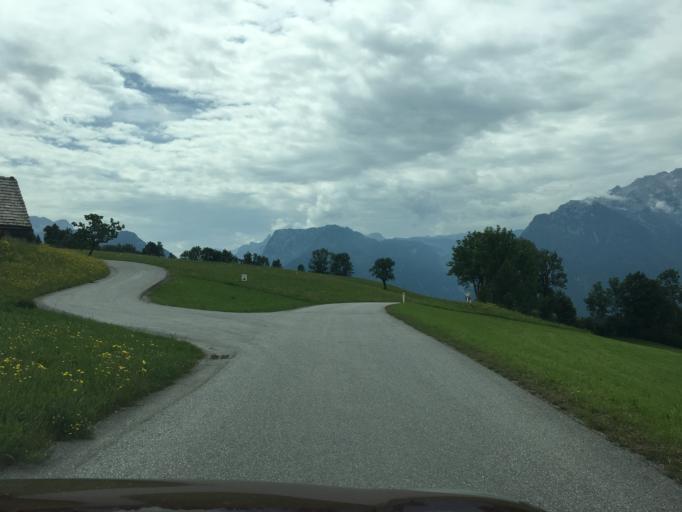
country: AT
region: Salzburg
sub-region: Politischer Bezirk Hallein
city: Golling an der Salzach
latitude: 47.6294
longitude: 13.1981
